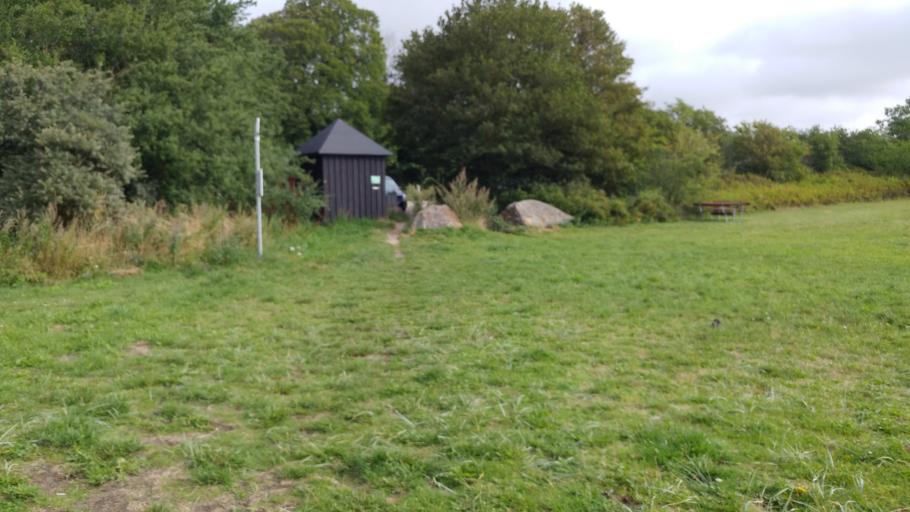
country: DK
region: Central Jutland
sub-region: Syddjurs Kommune
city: Ronde
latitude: 56.2917
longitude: 10.4159
